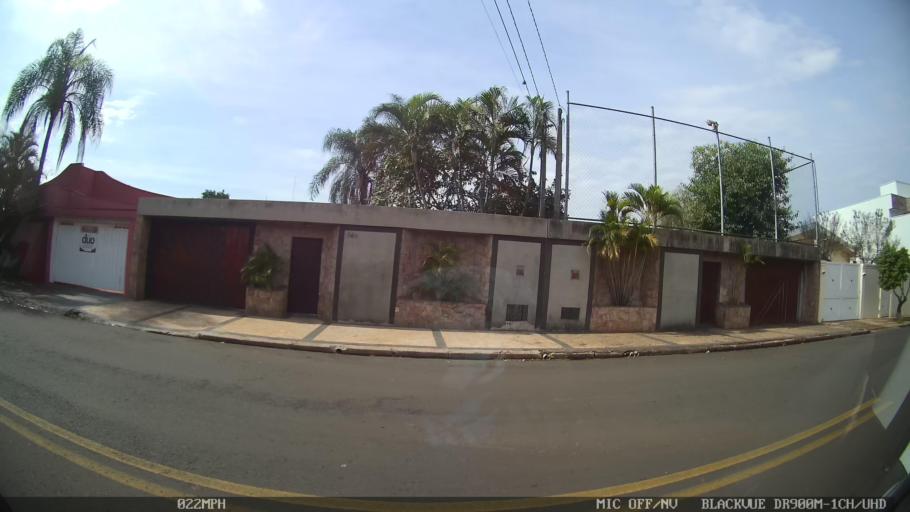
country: BR
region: Sao Paulo
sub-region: Piracicaba
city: Piracicaba
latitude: -22.7054
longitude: -47.6723
